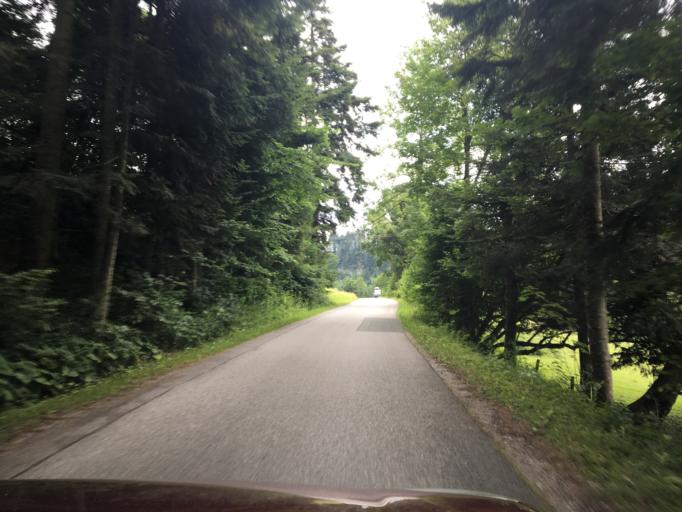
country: AT
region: Salzburg
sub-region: Politischer Bezirk Hallein
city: Golling an der Salzach
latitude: 47.6206
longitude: 13.1972
